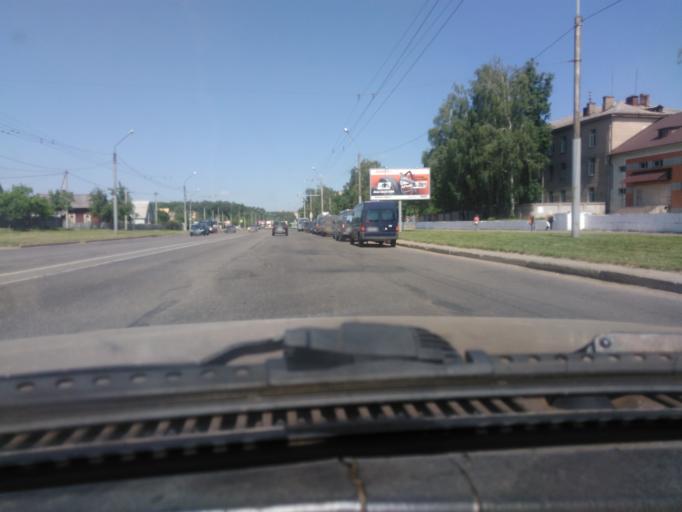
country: BY
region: Mogilev
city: Mahilyow
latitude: 53.9402
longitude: 30.3544
